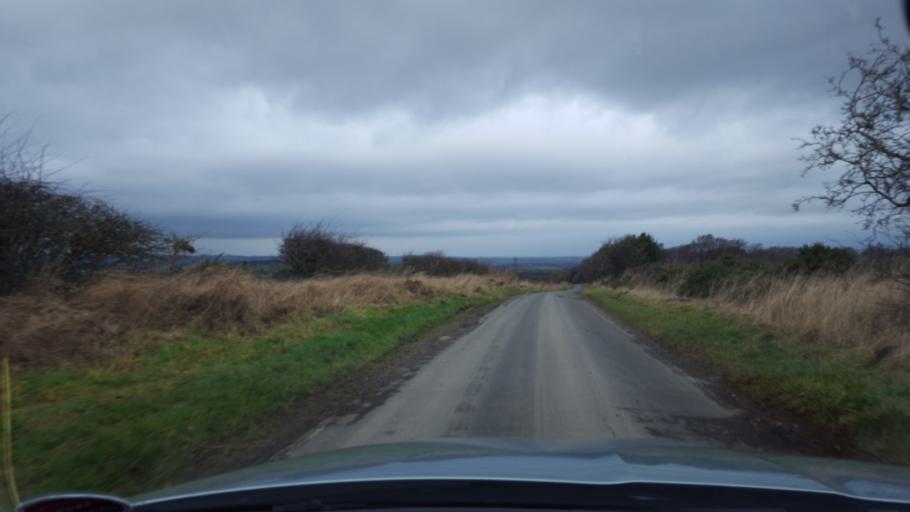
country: GB
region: Scotland
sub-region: West Lothian
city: Kirknewton
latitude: 55.8644
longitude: -3.4312
